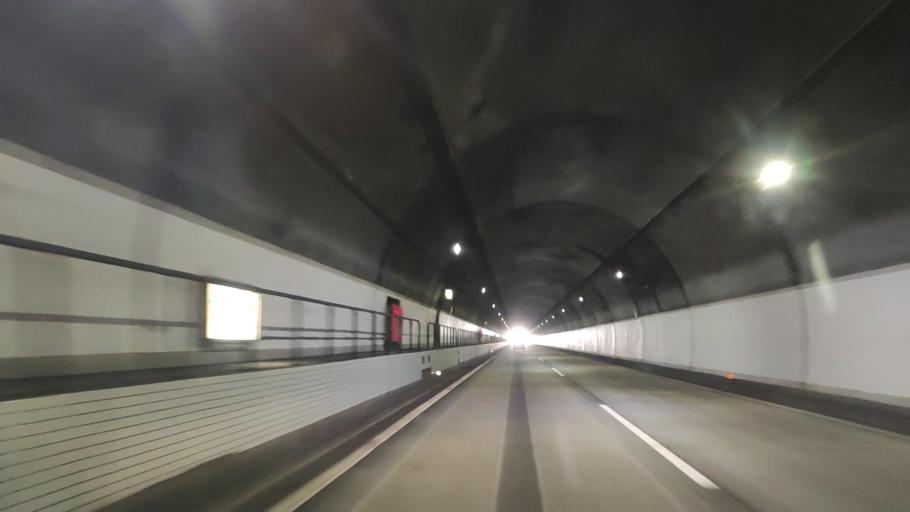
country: JP
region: Ehime
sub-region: Shikoku-chuo Shi
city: Matsuyama
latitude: 33.8209
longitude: 132.9658
